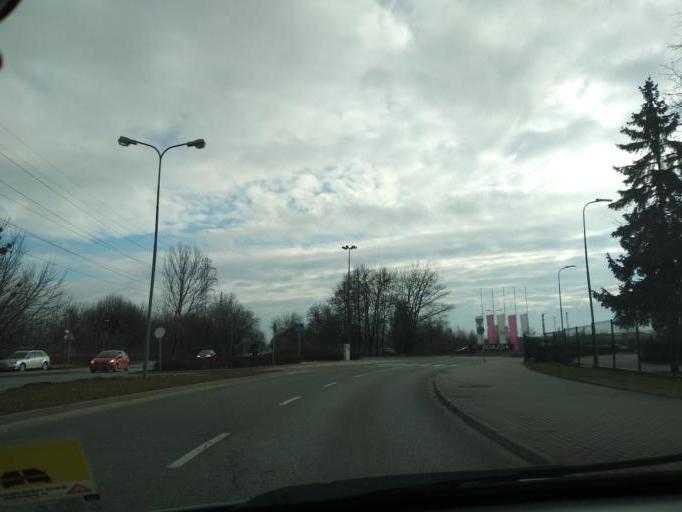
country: PL
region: Masovian Voivodeship
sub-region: Powiat piaseczynski
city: Piaseczno
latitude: 52.0884
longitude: 21.0227
